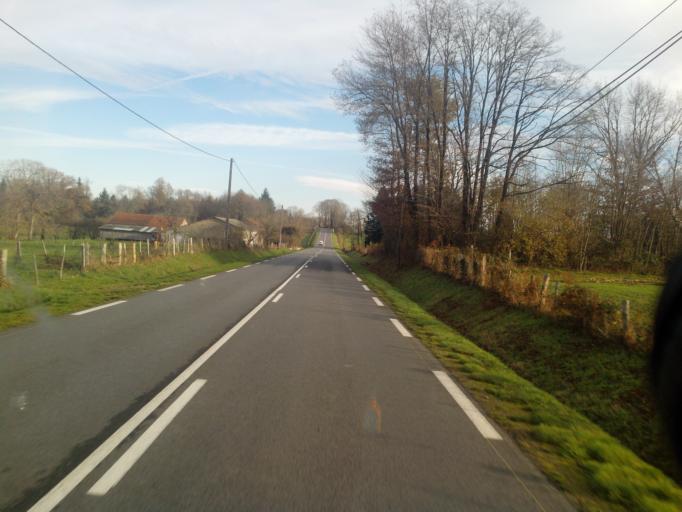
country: FR
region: Limousin
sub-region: Departement de la Haute-Vienne
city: Saint-Leonard-de-Noblat
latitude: 45.7827
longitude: 1.4808
